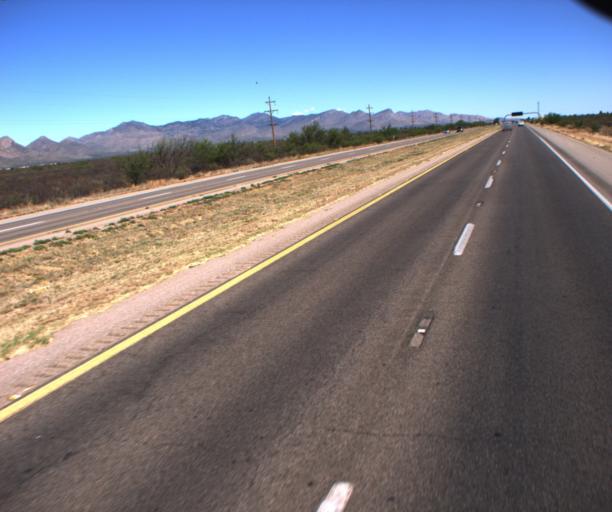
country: US
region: Arizona
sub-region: Cochise County
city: Huachuca City
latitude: 31.6657
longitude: -110.3502
